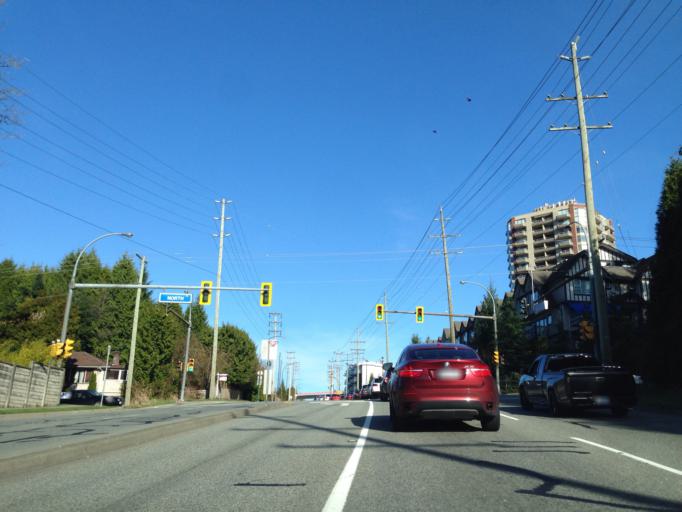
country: CA
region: British Columbia
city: Port Moody
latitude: 49.2628
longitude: -122.8938
